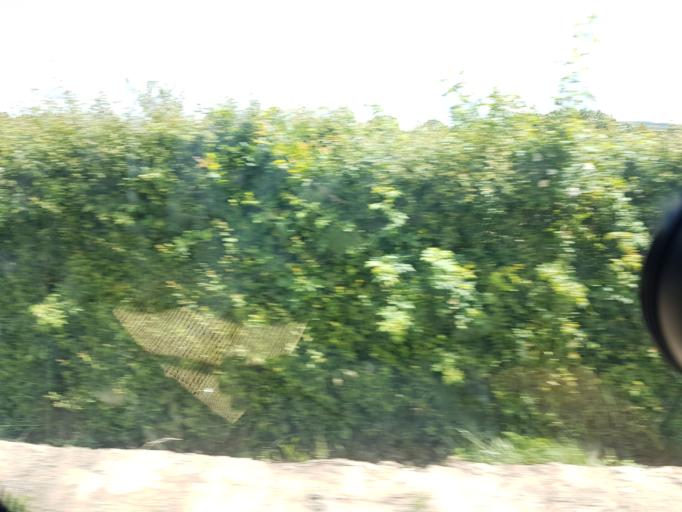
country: FR
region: Bourgogne
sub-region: Departement de Saone-et-Loire
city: Epinac
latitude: 46.9789
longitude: 4.4899
